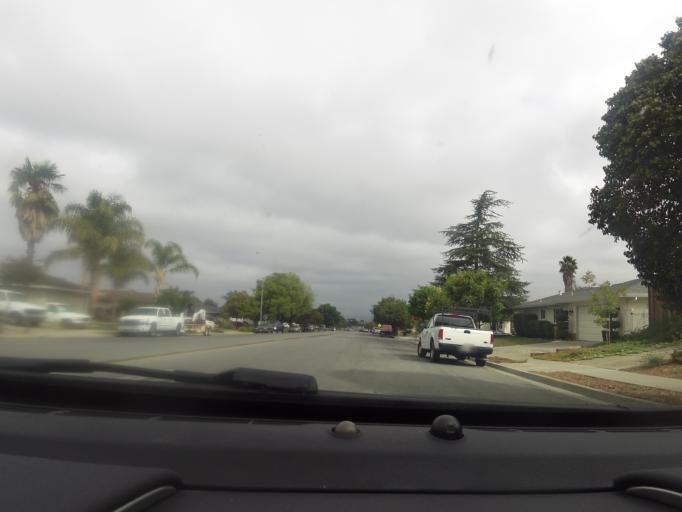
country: US
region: California
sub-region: San Benito County
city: Hollister
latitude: 36.8361
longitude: -121.3845
